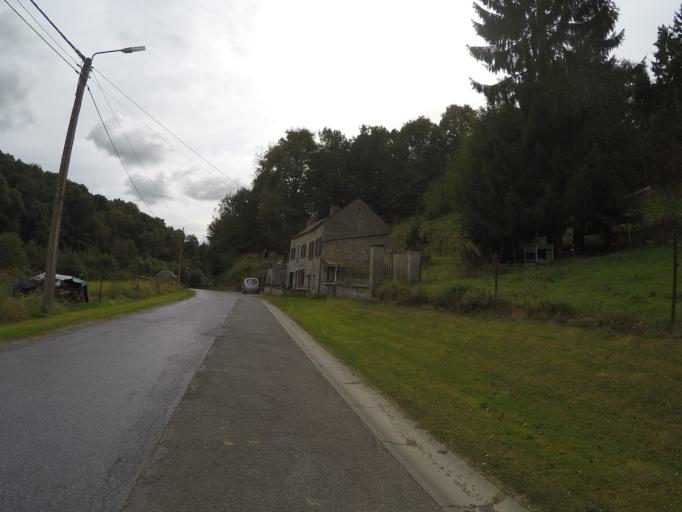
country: BE
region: Wallonia
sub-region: Province de Namur
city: Dinant
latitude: 50.2756
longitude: 4.9865
